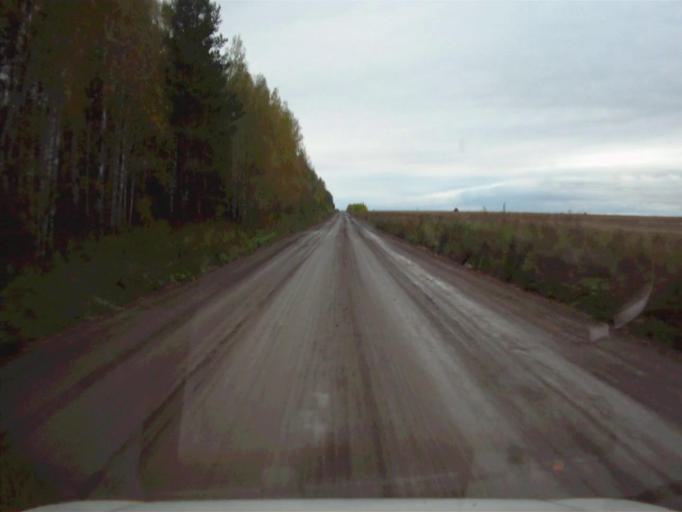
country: RU
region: Sverdlovsk
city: Mikhaylovsk
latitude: 56.1510
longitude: 59.2687
